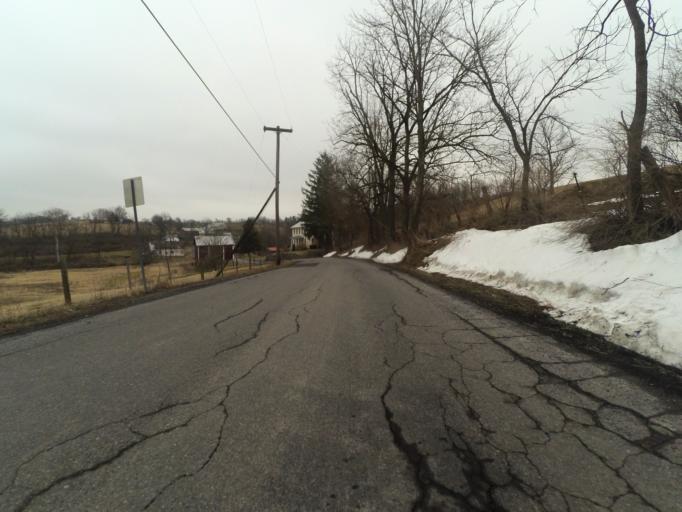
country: US
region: Pennsylvania
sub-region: Centre County
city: Centre Hall
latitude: 40.8664
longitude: -77.6111
